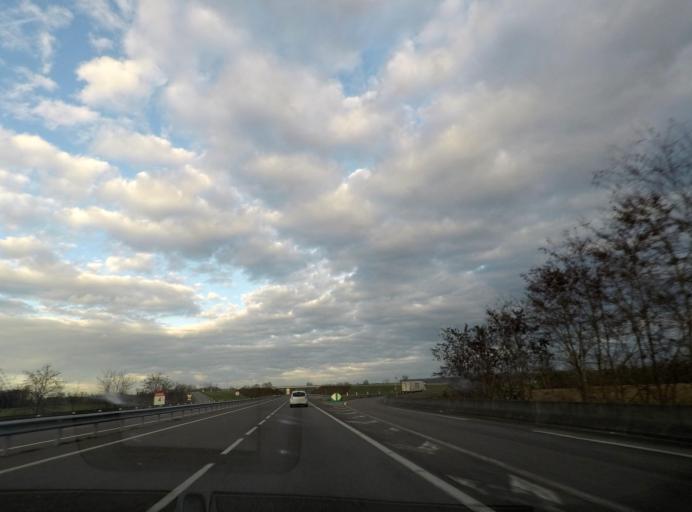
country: FR
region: Rhone-Alpes
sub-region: Departement de l'Ain
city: Crottet
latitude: 46.2816
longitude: 4.8648
